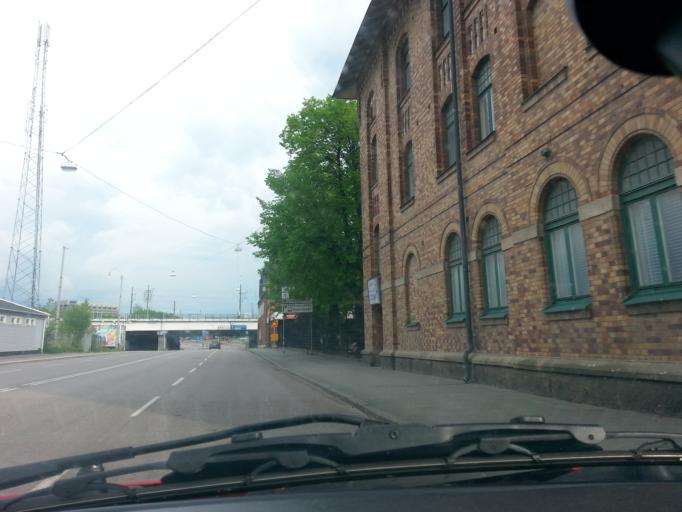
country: SE
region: Vaestra Goetaland
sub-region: Goteborg
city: Goeteborg
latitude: 57.7300
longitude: 12.0023
